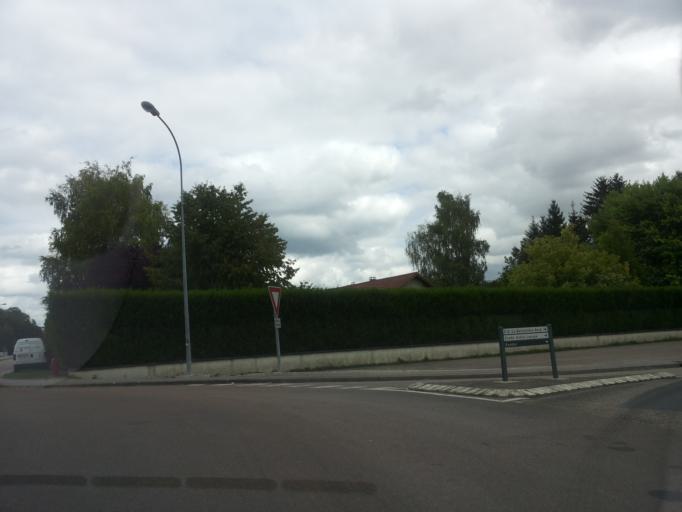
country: FR
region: Lorraine
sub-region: Departement de la Meuse
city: Ligny-en-Barrois
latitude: 48.6758
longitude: 5.3257
